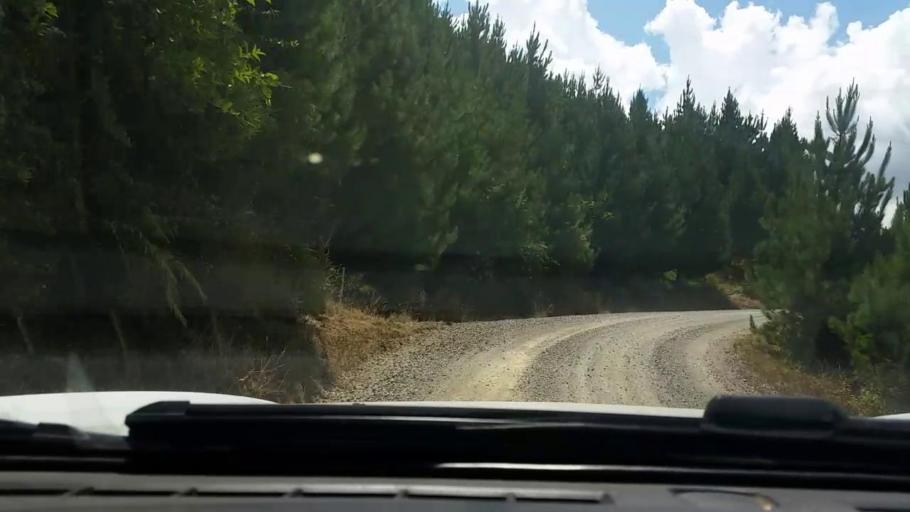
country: NZ
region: Bay of Plenty
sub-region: Kawerau District
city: Kawerau
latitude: -38.0322
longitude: 176.5534
